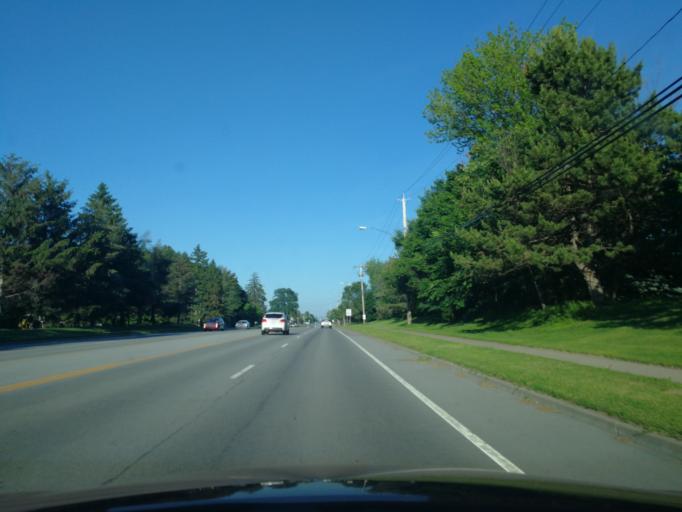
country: US
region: New York
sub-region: Monroe County
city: Greece
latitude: 43.2530
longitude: -77.7051
